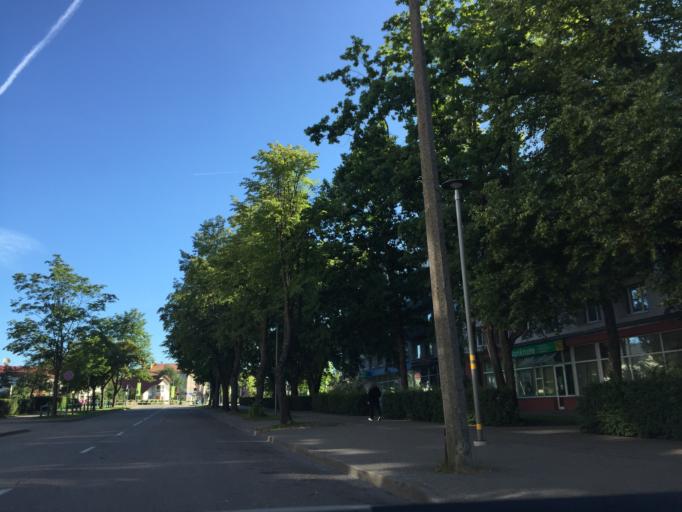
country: LV
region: Ventspils
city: Ventspils
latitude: 57.4026
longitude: 21.5902
